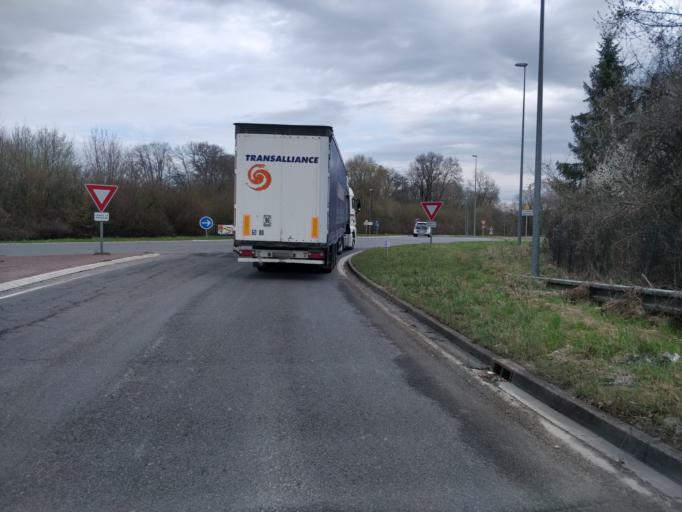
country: FR
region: Lorraine
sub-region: Departement de la Moselle
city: Gandrange
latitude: 49.2825
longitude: 6.1252
